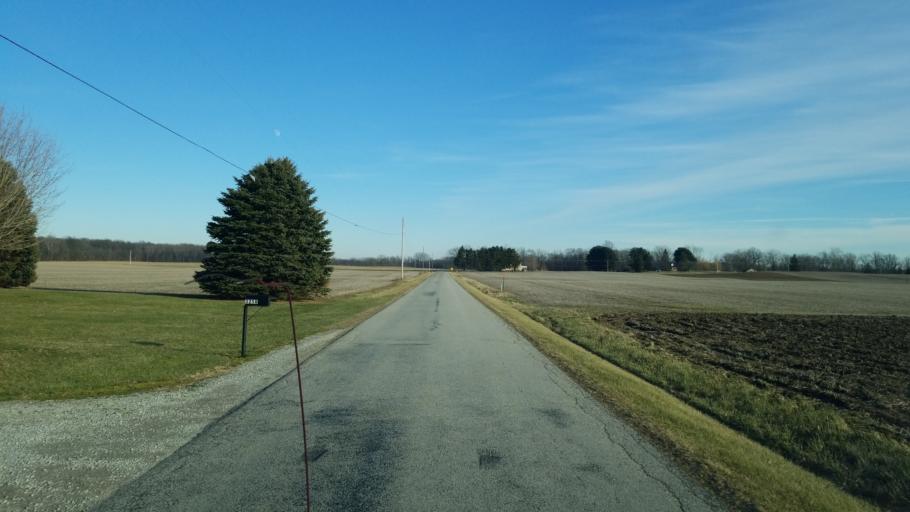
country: US
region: Ohio
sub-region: Huron County
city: Monroeville
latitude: 41.1847
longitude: -82.7077
